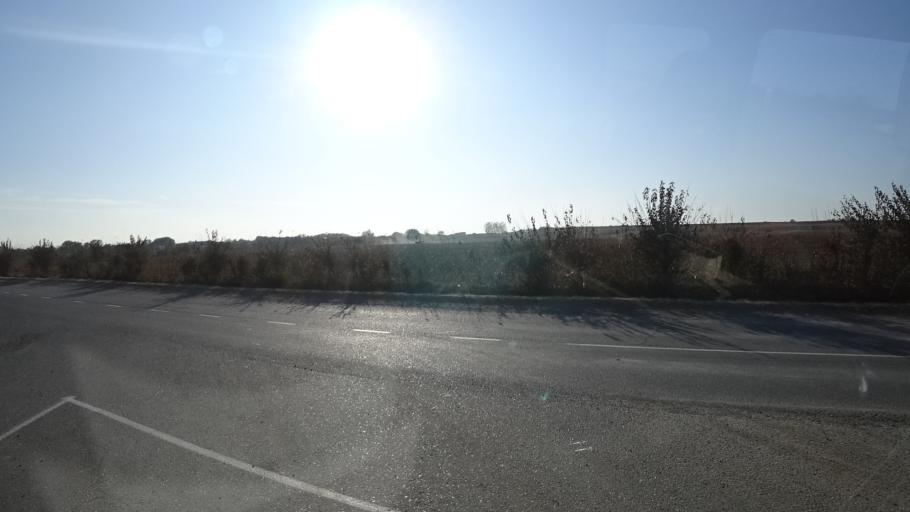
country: UZ
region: Navoiy
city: Beshrabot
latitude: 40.2182
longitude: 65.3830
